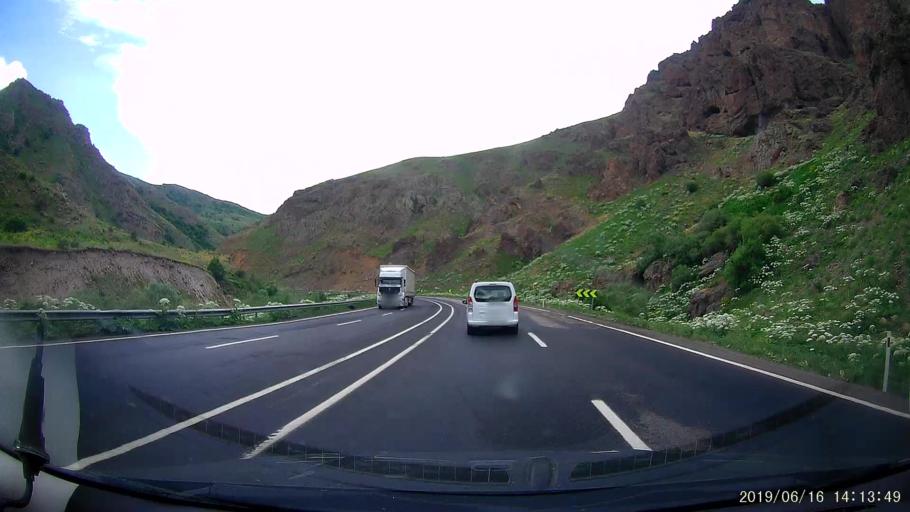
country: TR
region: Agri
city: Tahir
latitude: 39.7962
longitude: 42.5087
